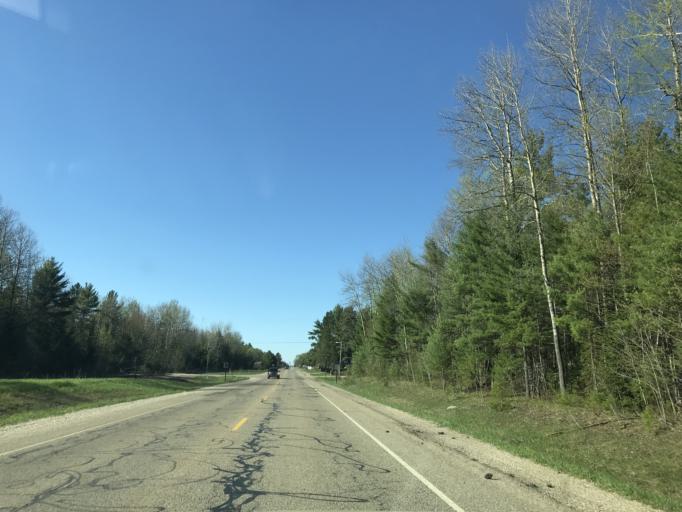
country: US
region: Michigan
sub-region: Crawford County
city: Grayling
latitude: 44.7700
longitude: -84.7544
